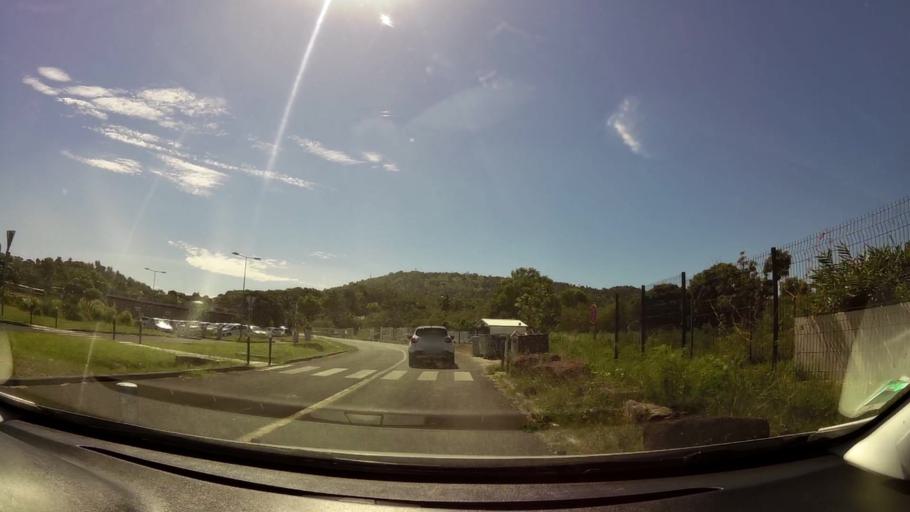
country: YT
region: Pamandzi
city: Pamandzi
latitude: -12.8037
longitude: 45.2836
